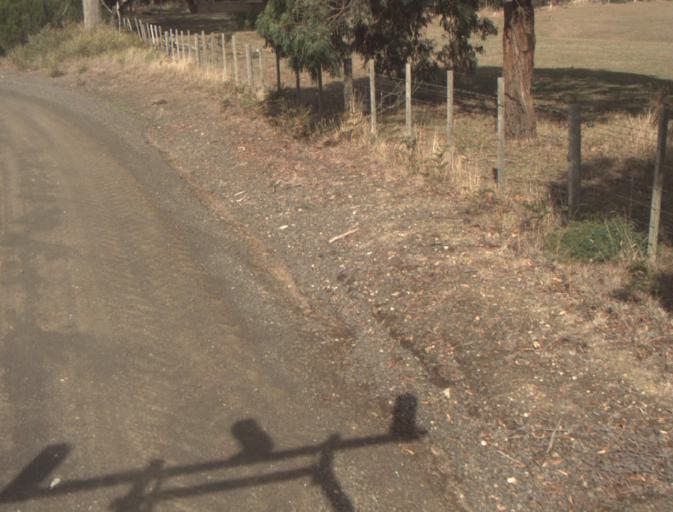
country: AU
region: Tasmania
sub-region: Launceston
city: Mayfield
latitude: -41.2187
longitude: 147.1665
